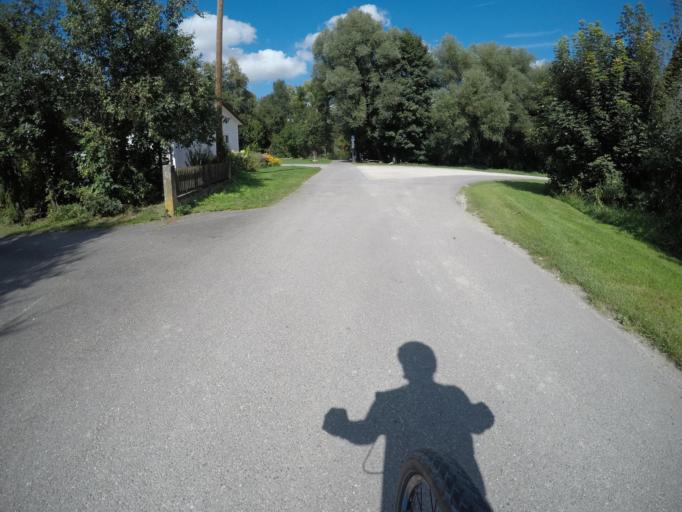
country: DE
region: Bavaria
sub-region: Swabia
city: Wittislingen
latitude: 48.6054
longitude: 10.4528
